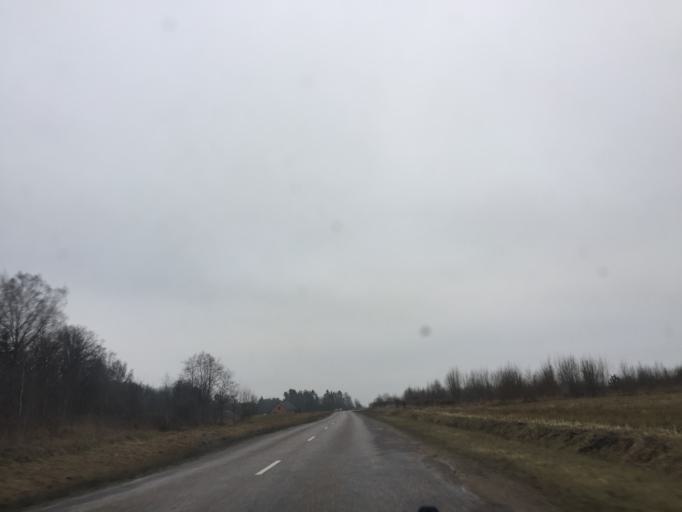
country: LV
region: Limbazu Rajons
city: Limbazi
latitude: 57.5344
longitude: 24.6874
